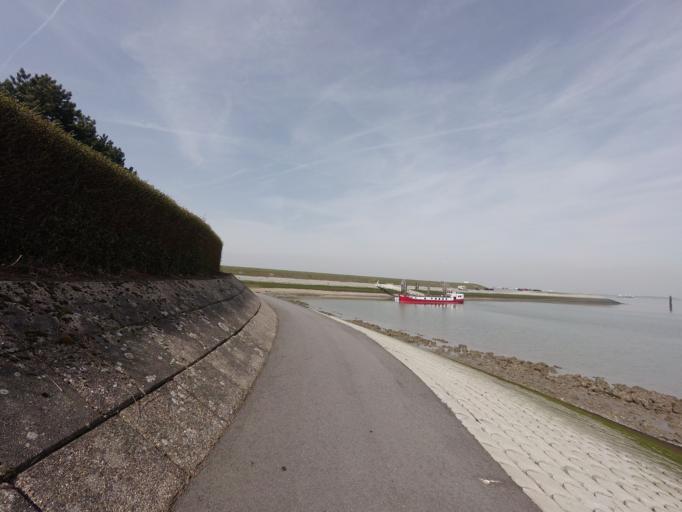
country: NL
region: Zeeland
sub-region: Gemeente Reimerswaal
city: Yerseke
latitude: 51.3983
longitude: 4.0172
